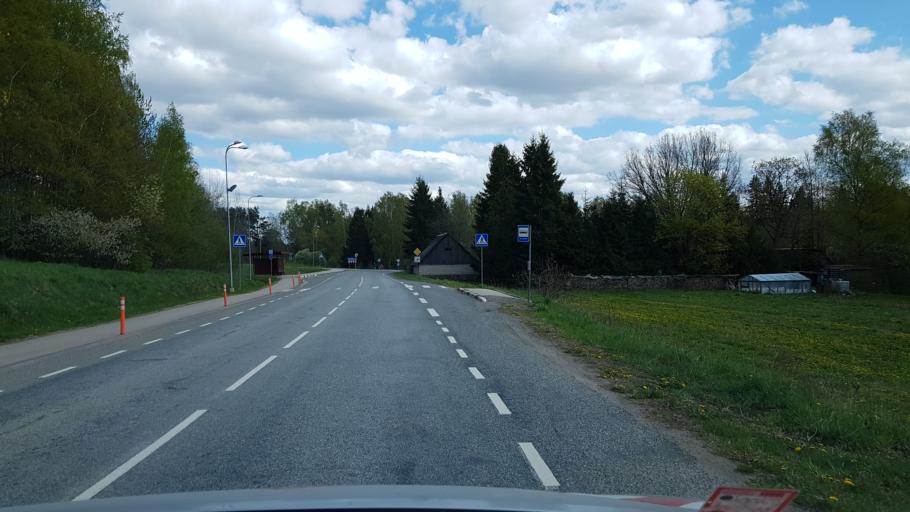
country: EE
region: Tartu
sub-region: UElenurme vald
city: Ulenurme
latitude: 58.2940
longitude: 26.8904
